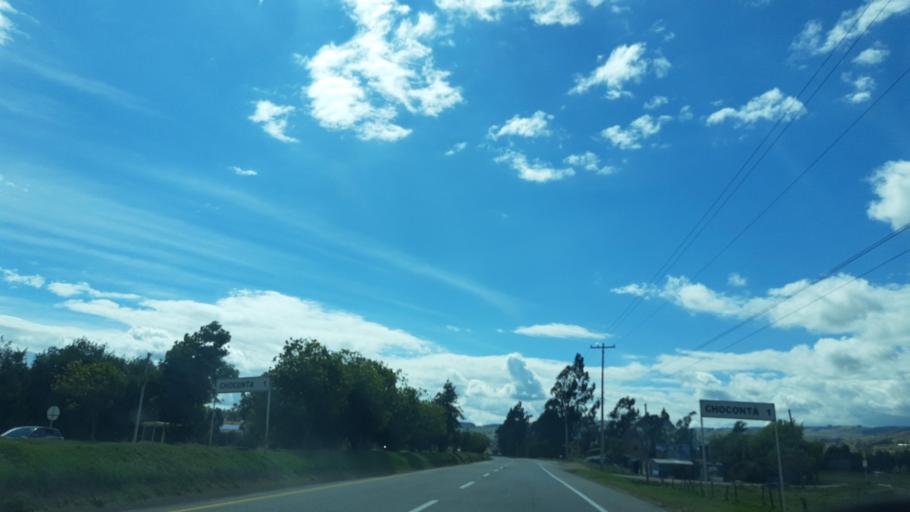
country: CO
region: Cundinamarca
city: Choconta
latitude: 5.1552
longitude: -73.6691
